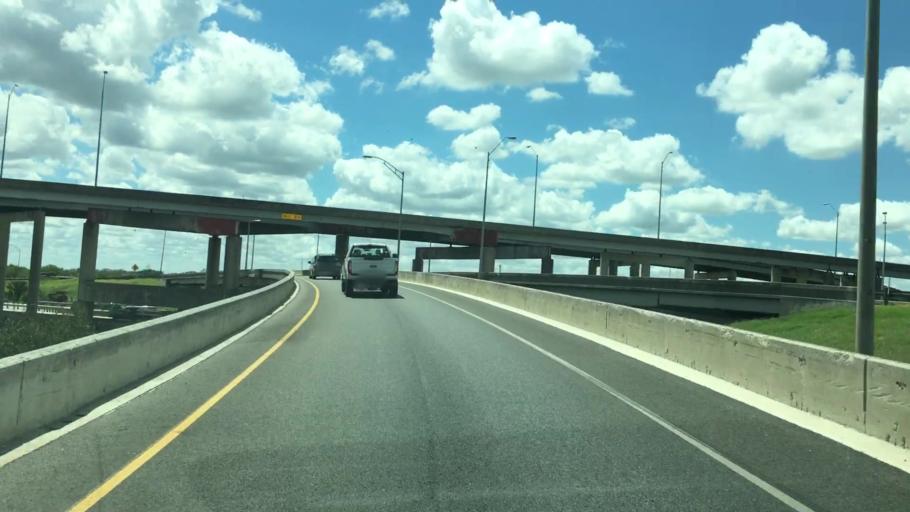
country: US
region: Texas
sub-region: Bexar County
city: China Grove
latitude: 29.3302
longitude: -98.4154
